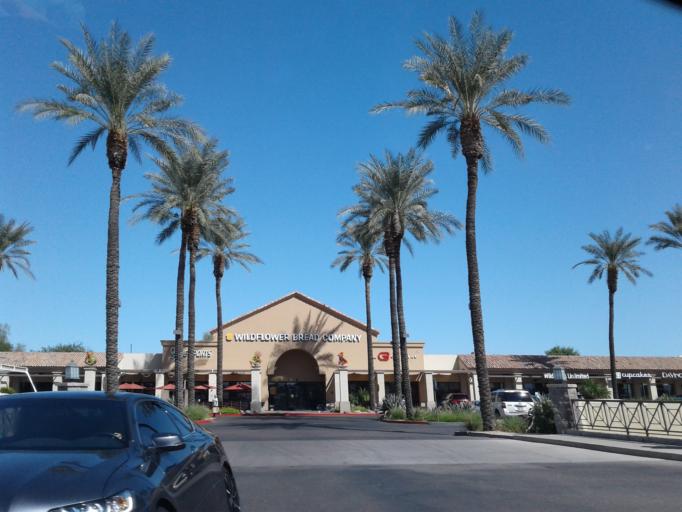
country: US
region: Arizona
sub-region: Maricopa County
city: Paradise Valley
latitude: 33.5387
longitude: -111.9233
